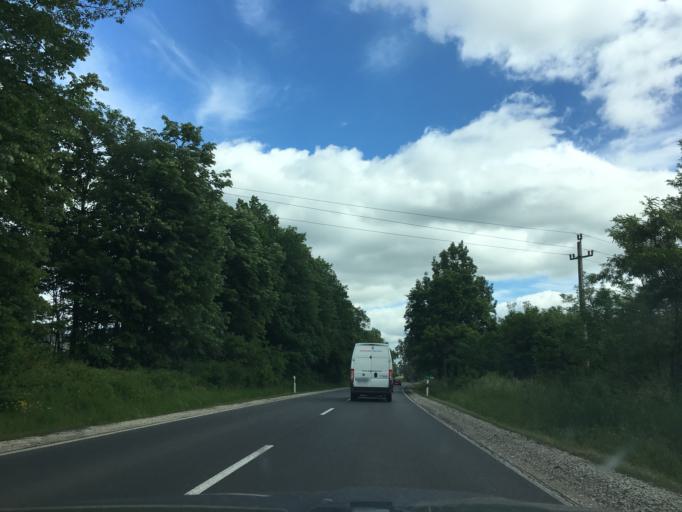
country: HU
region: Borsod-Abauj-Zemplen
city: Tarcal
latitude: 48.1807
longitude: 21.3501
